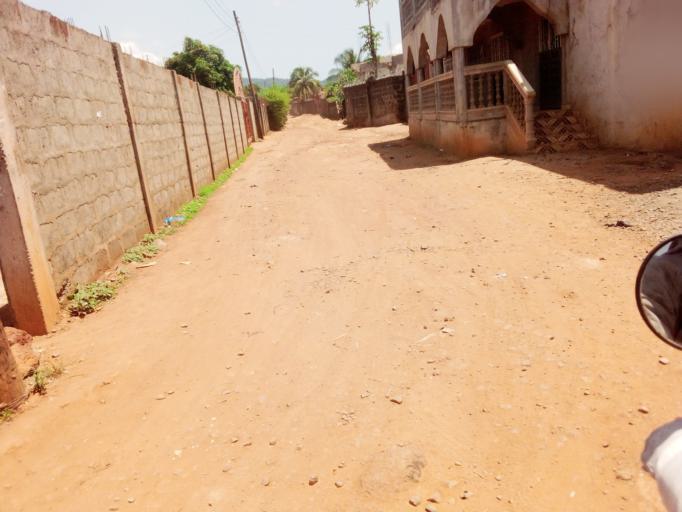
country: SL
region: Western Area
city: Waterloo
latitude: 8.3330
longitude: -13.0741
